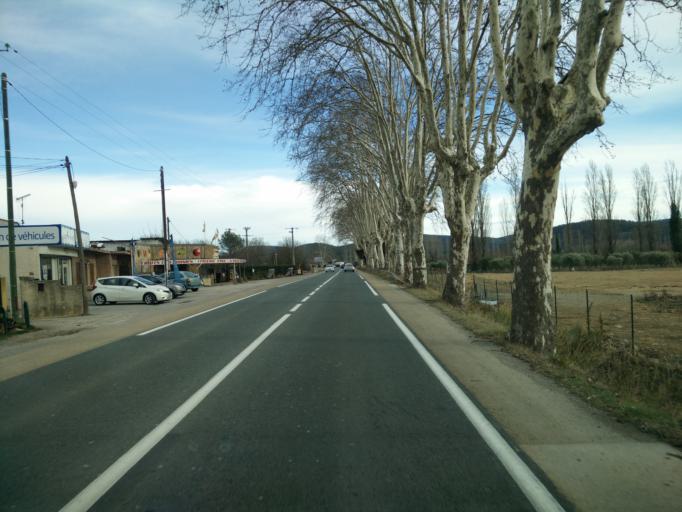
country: FR
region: Provence-Alpes-Cote d'Azur
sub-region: Departement du Var
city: Les Arcs
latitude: 43.4476
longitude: 6.4791
